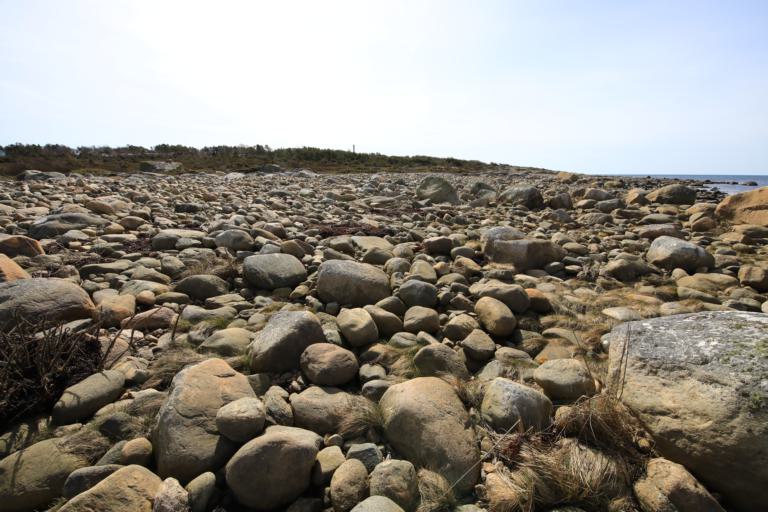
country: SE
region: Halland
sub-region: Kungsbacka Kommun
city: Frillesas
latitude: 57.2739
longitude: 12.1147
